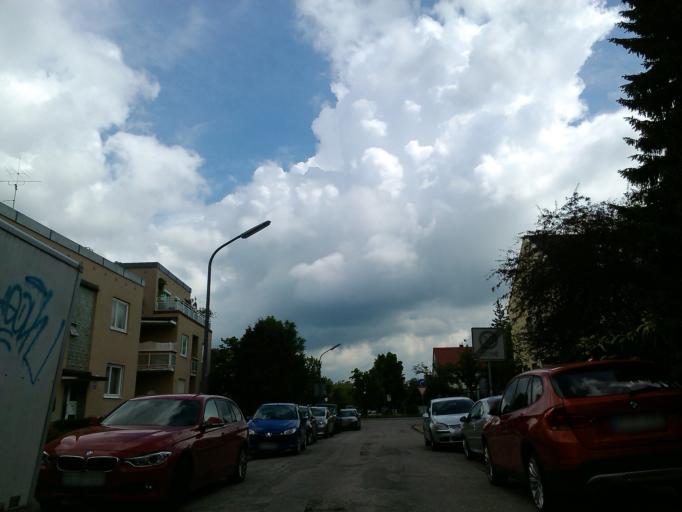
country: DE
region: Bavaria
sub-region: Upper Bavaria
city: Neubiberg
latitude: 48.1238
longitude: 11.6554
